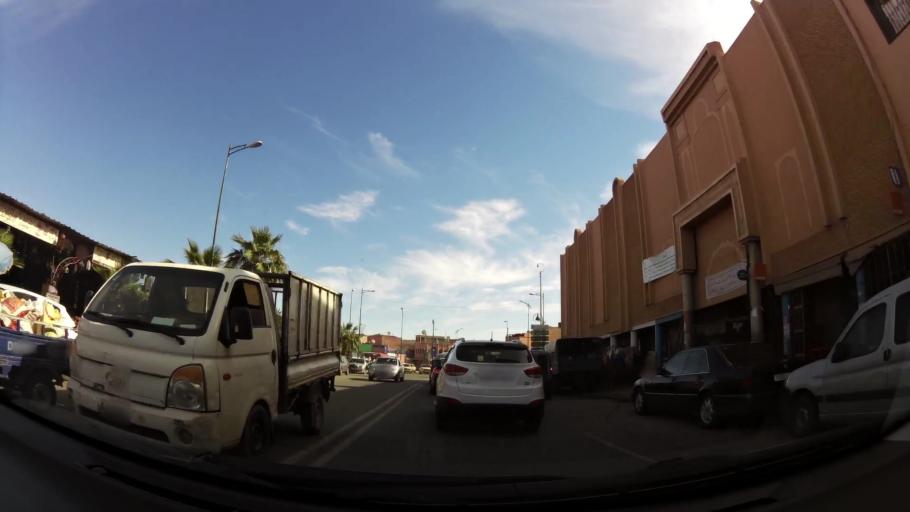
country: MA
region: Marrakech-Tensift-Al Haouz
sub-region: Marrakech
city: Marrakesh
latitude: 31.6233
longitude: -7.9708
